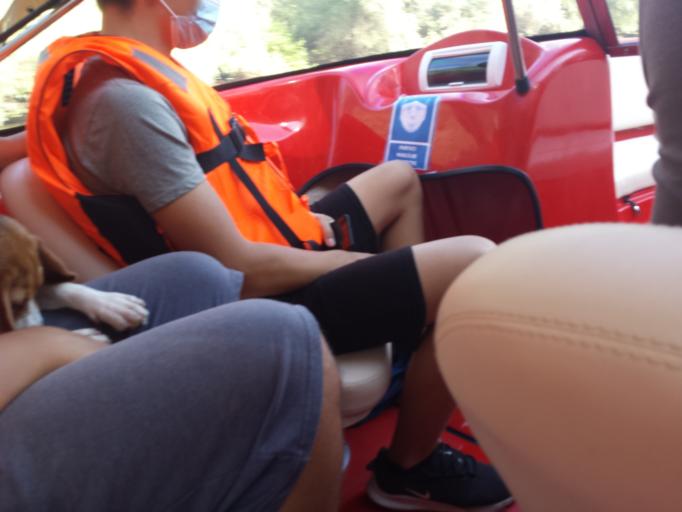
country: RO
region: Tulcea
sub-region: Comuna Pardina
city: Pardina
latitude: 45.2431
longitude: 28.9208
